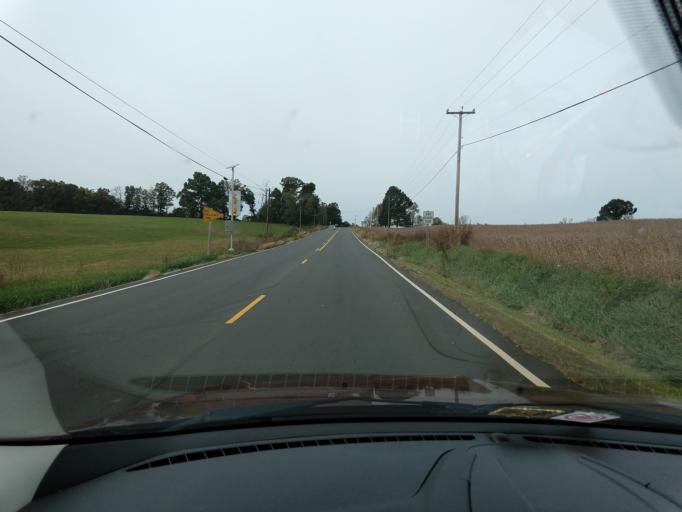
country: US
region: Virginia
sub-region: Franklin County
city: Union Hall
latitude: 36.9885
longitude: -79.7582
